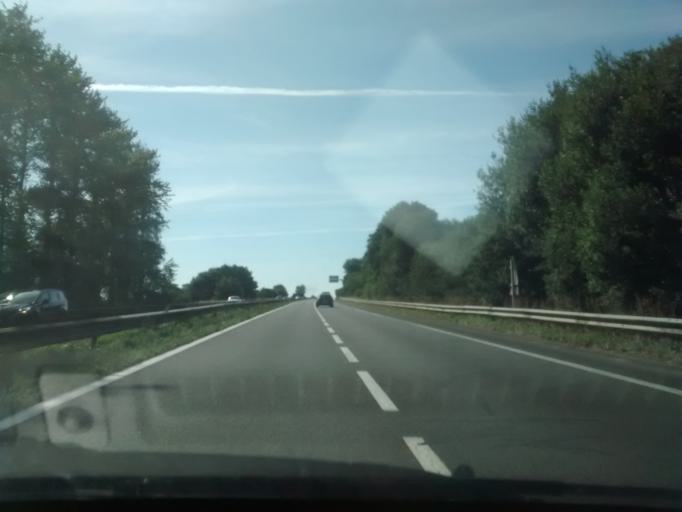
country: FR
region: Brittany
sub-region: Departement des Cotes-d'Armor
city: Plouagat
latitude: 48.5316
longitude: -3.0022
